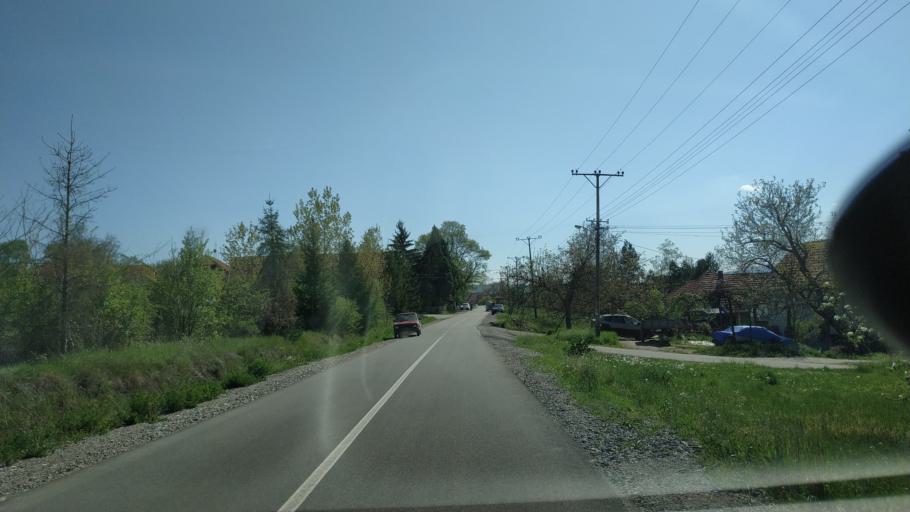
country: RS
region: Central Serbia
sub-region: Nisavski Okrug
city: Nis
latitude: 43.4545
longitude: 21.8515
